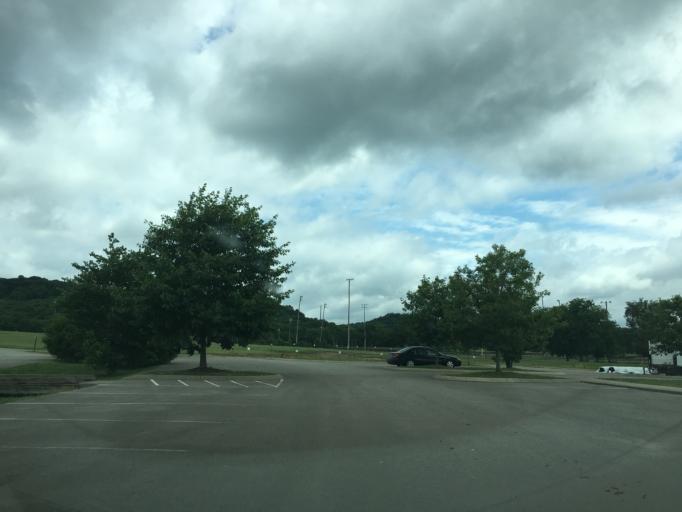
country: US
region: Tennessee
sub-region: Davidson County
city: Forest Hills
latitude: 36.0506
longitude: -86.8981
